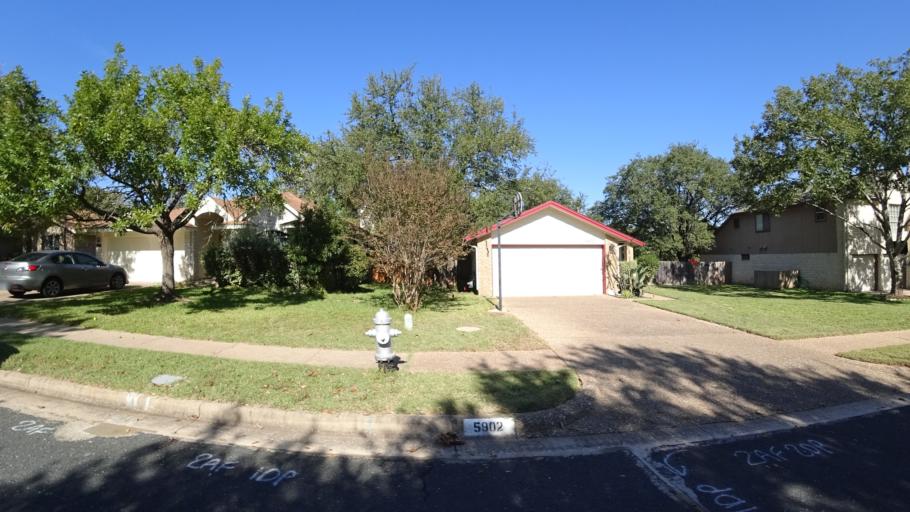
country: US
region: Texas
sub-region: Travis County
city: Shady Hollow
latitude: 30.2158
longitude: -97.8694
